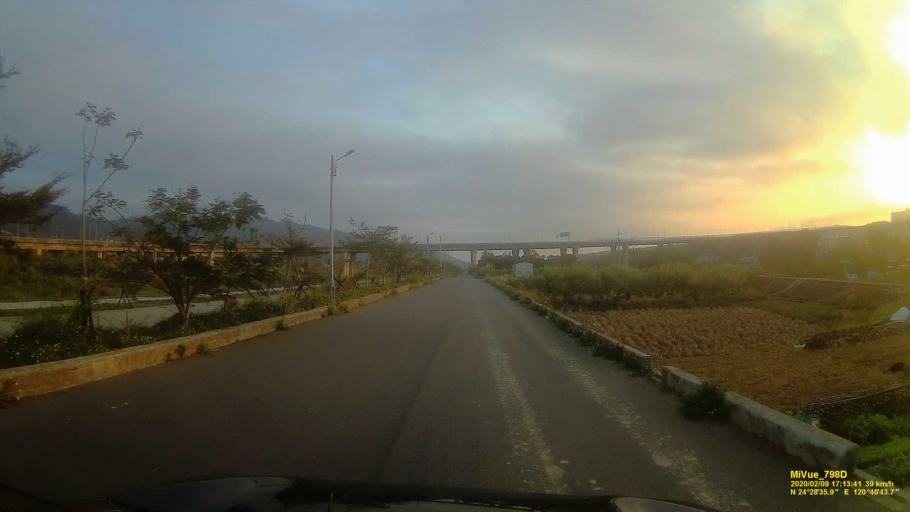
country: TW
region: Taiwan
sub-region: Miaoli
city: Miaoli
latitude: 24.4765
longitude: 120.7788
